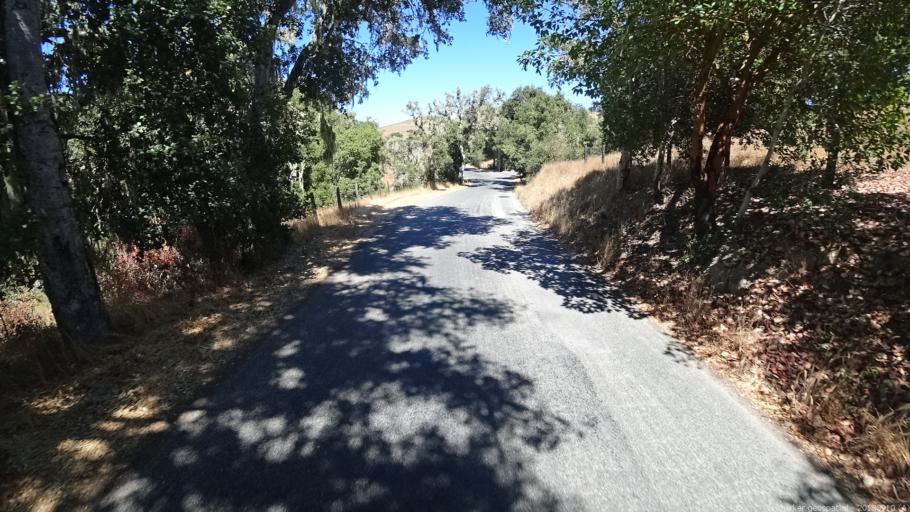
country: US
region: California
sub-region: Monterey County
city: Carmel Valley Village
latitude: 36.4650
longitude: -121.7991
